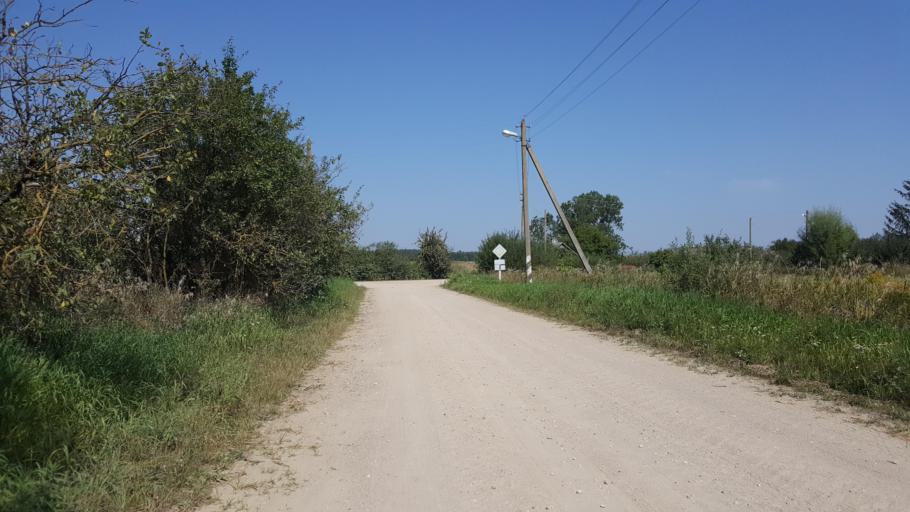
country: PL
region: Podlasie
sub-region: Powiat hajnowski
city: Czeremcha
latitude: 52.4668
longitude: 23.4509
